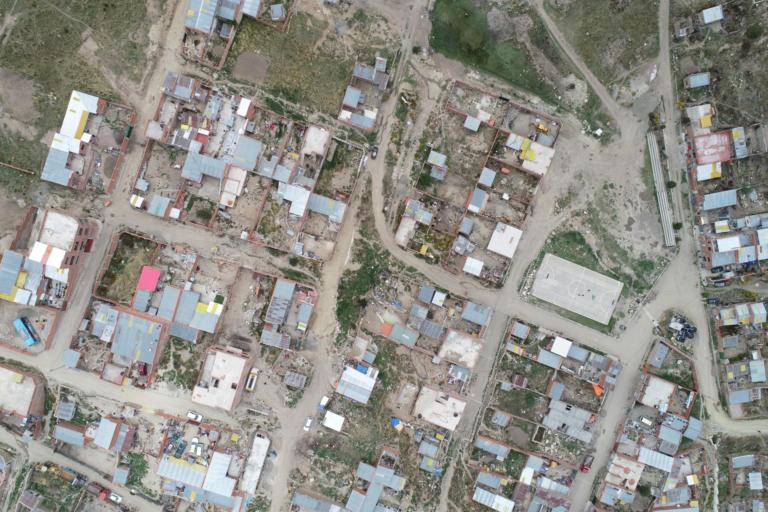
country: BO
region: La Paz
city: La Paz
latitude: -16.4449
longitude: -68.1430
